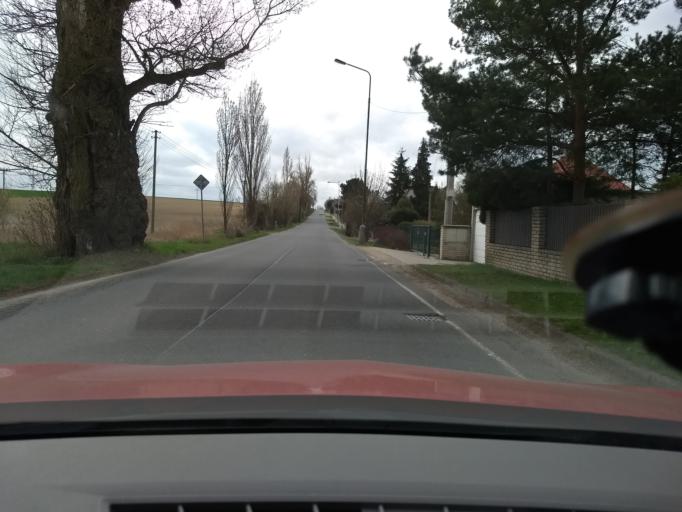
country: CZ
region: Central Bohemia
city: Unhost'
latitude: 50.0846
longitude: 14.1390
